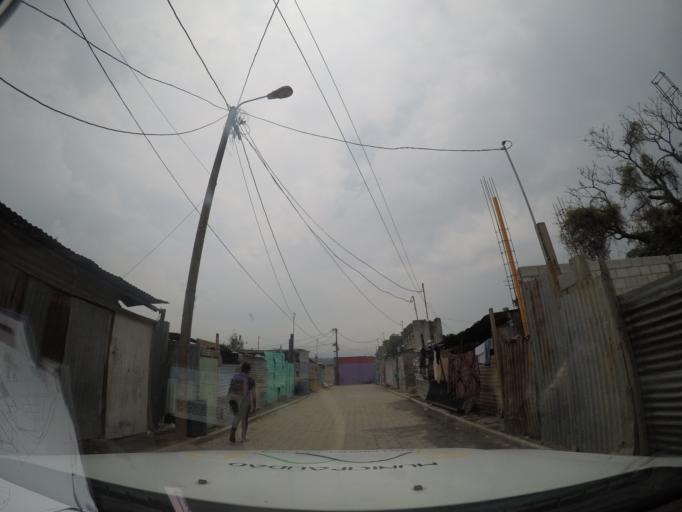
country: GT
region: Guatemala
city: Petapa
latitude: 14.5048
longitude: -90.5492
